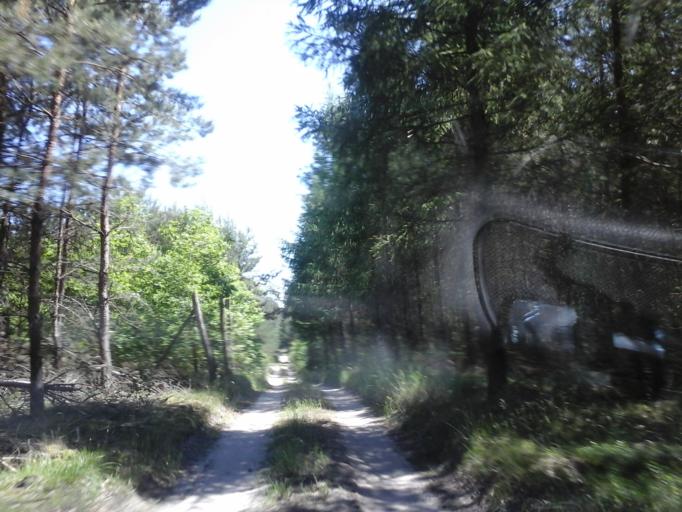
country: PL
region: West Pomeranian Voivodeship
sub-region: Powiat walecki
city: Czlopa
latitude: 53.1306
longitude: 15.9532
